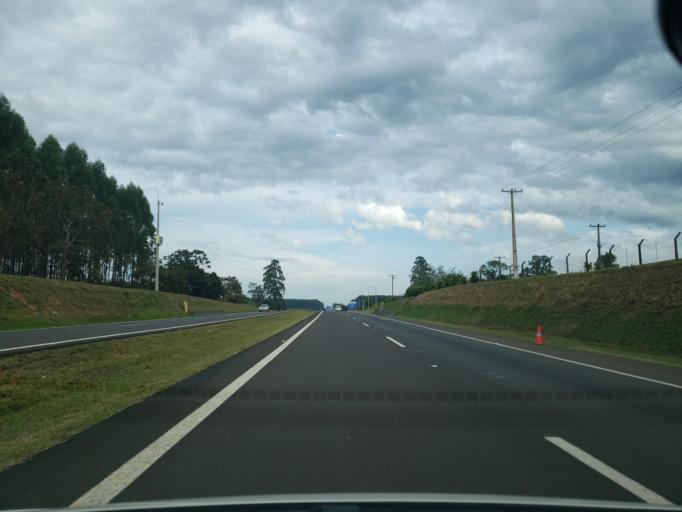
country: BR
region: Sao Paulo
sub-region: Itirapina
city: Itirapina
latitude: -22.2599
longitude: -47.8779
